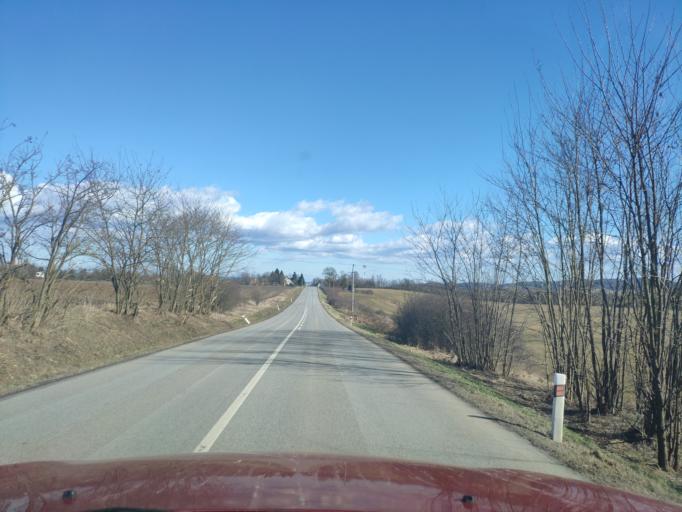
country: HU
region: Borsod-Abauj-Zemplen
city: Ozd
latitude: 48.2987
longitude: 20.1918
